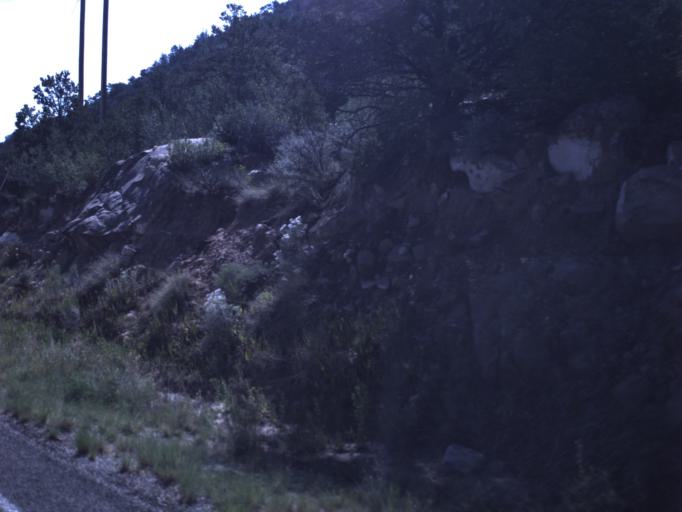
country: US
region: Utah
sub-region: Duchesne County
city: Duchesne
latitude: 40.2961
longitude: -110.5897
